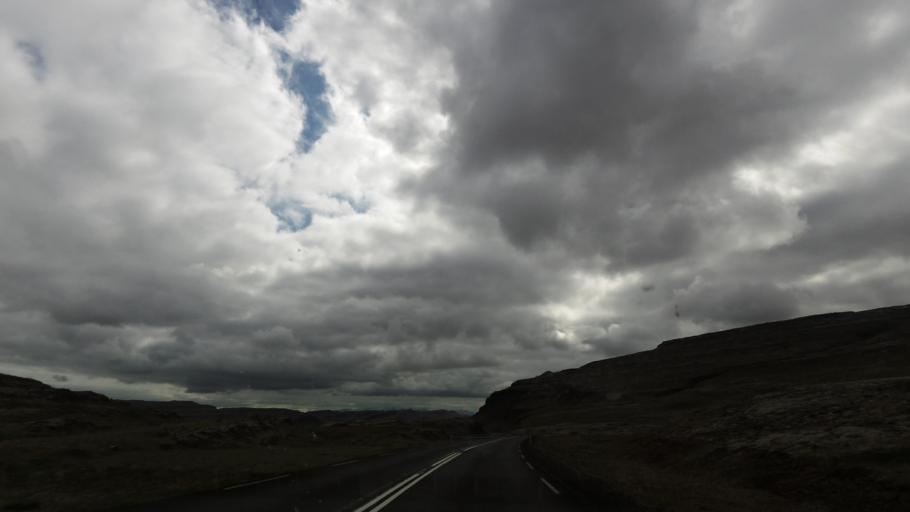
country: IS
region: West
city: Borgarnes
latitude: 64.8134
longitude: -21.4711
